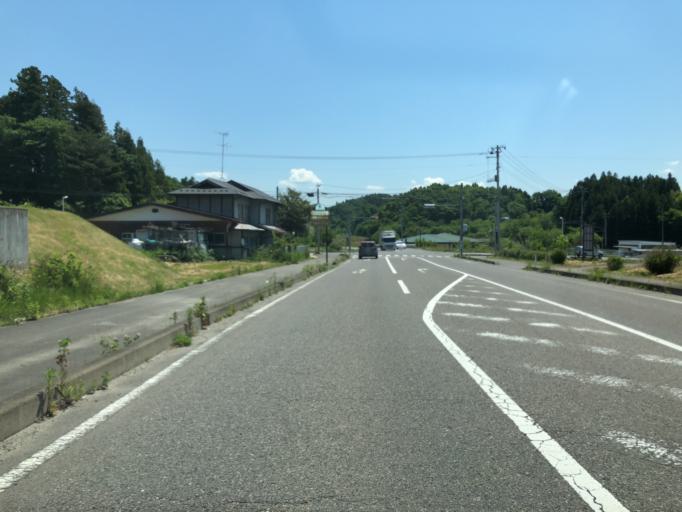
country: JP
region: Fukushima
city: Motomiya
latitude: 37.5255
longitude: 140.4435
